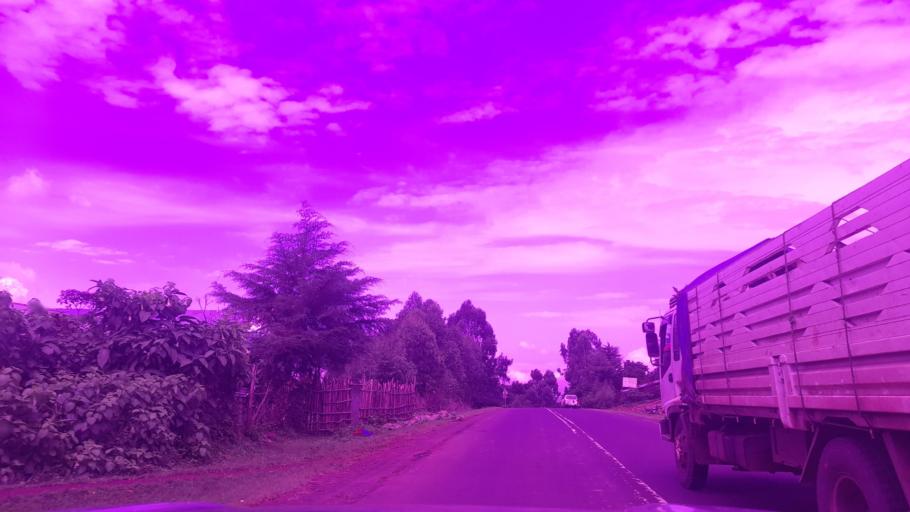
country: ET
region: Oromiya
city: Jima
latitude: 7.5218
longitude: 36.5371
